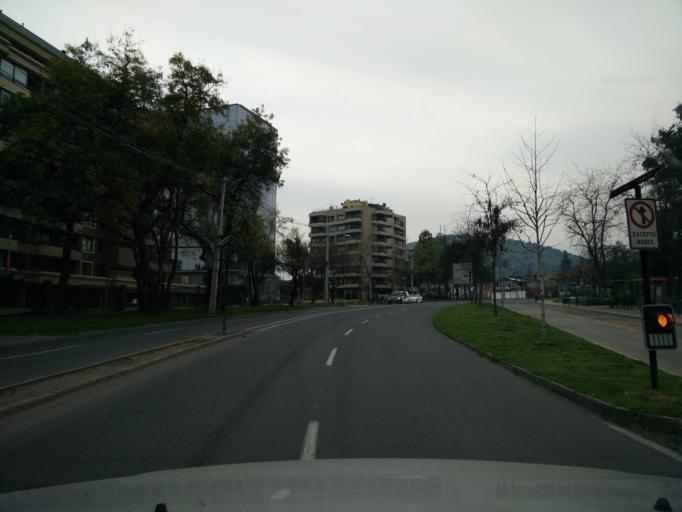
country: CL
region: Santiago Metropolitan
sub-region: Provincia de Santiago
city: Villa Presidente Frei, Nunoa, Santiago, Chile
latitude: -33.4073
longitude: -70.5449
